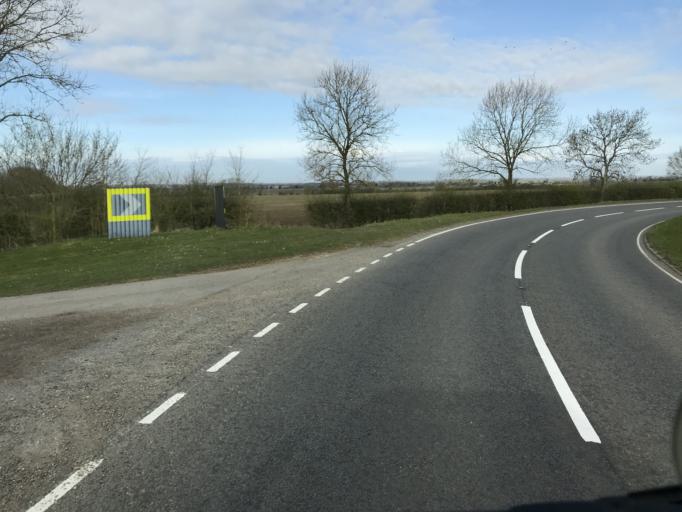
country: GB
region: England
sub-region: Lincolnshire
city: Market Rasen
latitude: 53.3949
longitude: -0.4176
